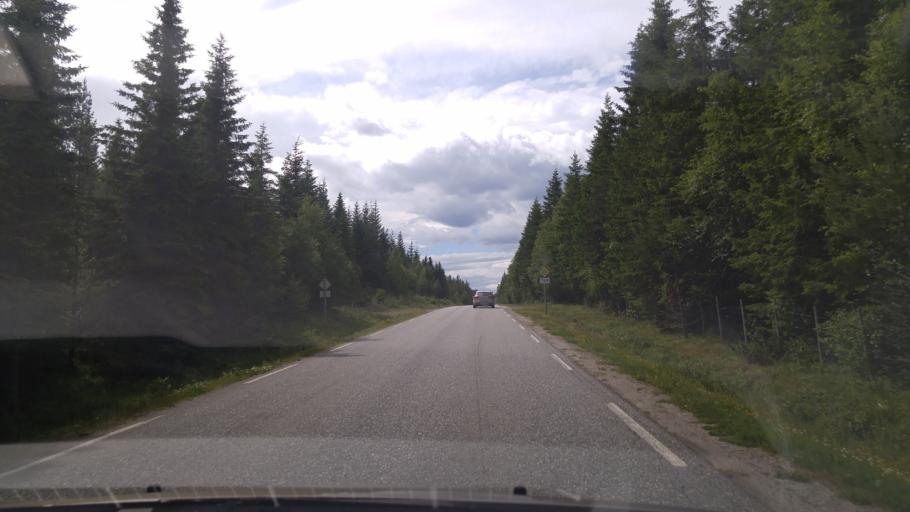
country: NO
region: Nord-Trondelag
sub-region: Naeroy
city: Kolvereid
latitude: 64.7249
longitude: 11.5049
